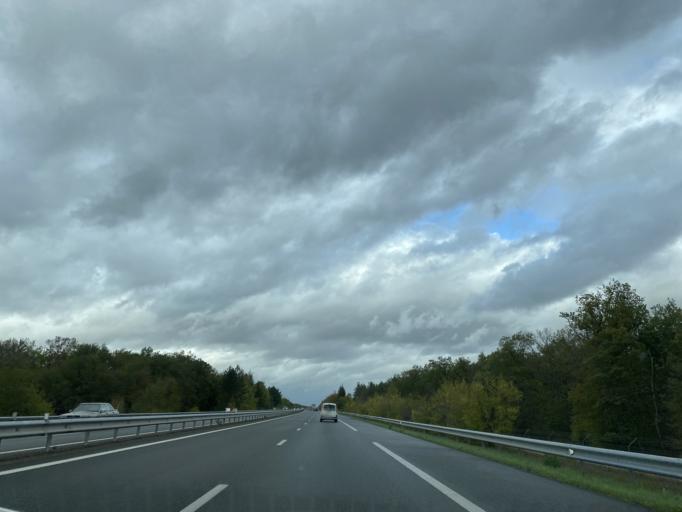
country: FR
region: Centre
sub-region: Departement du Cher
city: Levet
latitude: 46.8715
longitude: 2.4254
